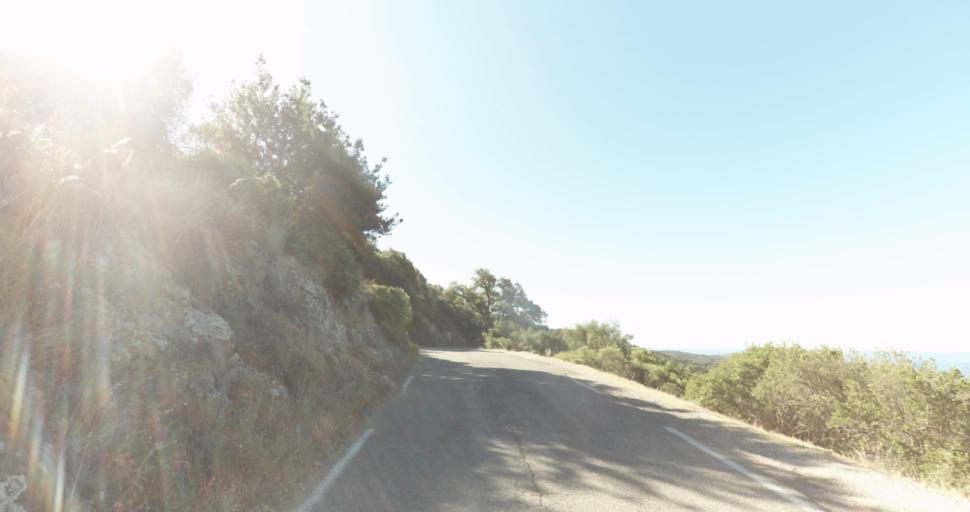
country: FR
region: Provence-Alpes-Cote d'Azur
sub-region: Departement du Var
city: Ramatuelle
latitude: 43.2171
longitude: 6.6003
